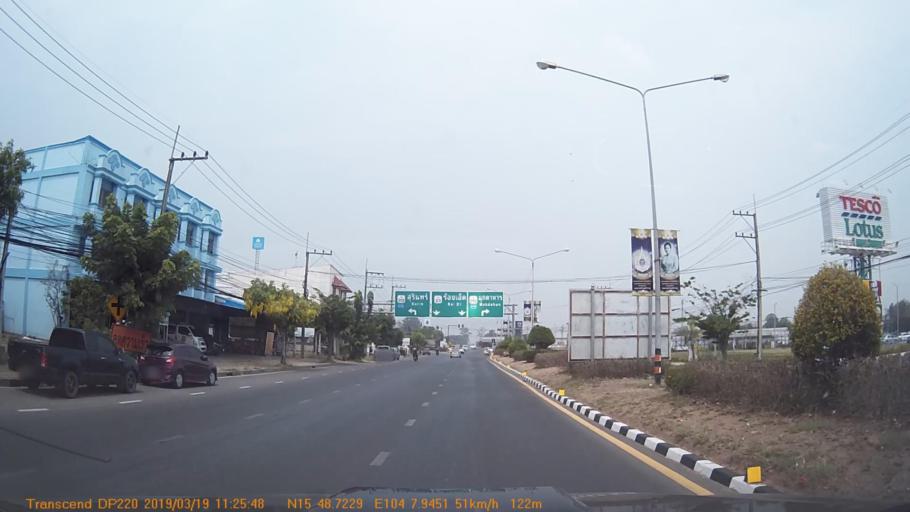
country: TH
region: Yasothon
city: Yasothon
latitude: 15.8123
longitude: 104.1322
